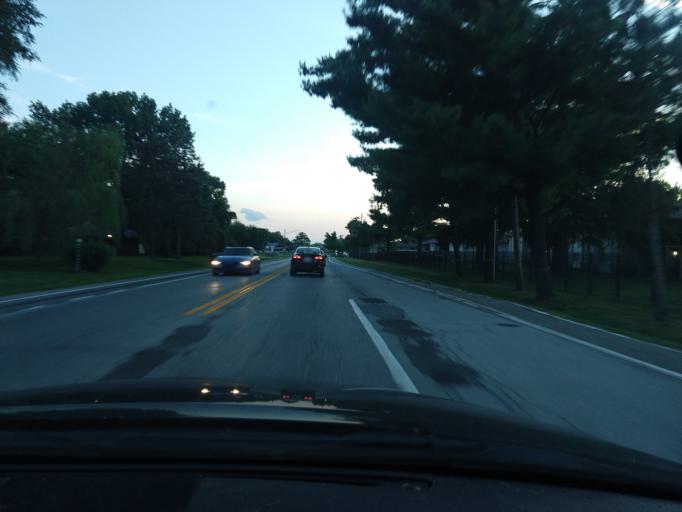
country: US
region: Indiana
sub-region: Marion County
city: Broad Ripple
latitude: 39.8430
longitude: -86.1150
